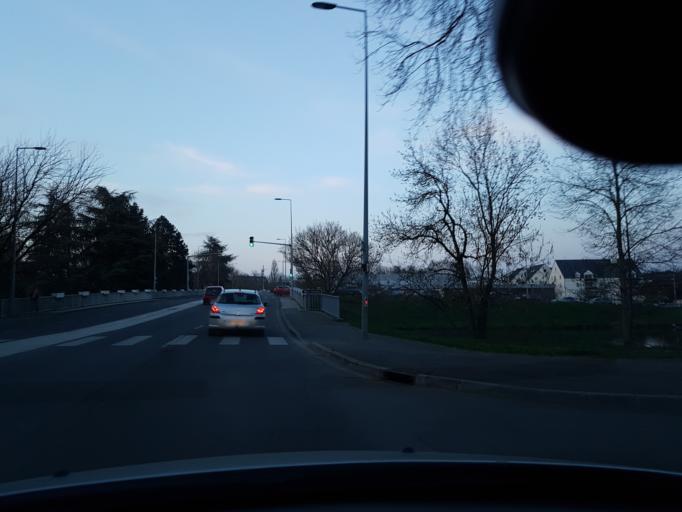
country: FR
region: Centre
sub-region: Departement du Cher
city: Bourges
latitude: 47.0907
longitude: 2.3986
